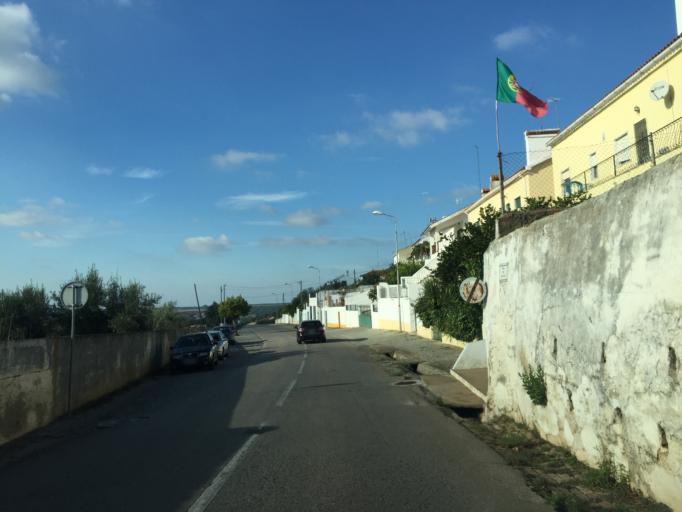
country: PT
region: Portalegre
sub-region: Fronteira
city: Fronteira
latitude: 39.0594
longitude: -7.6500
